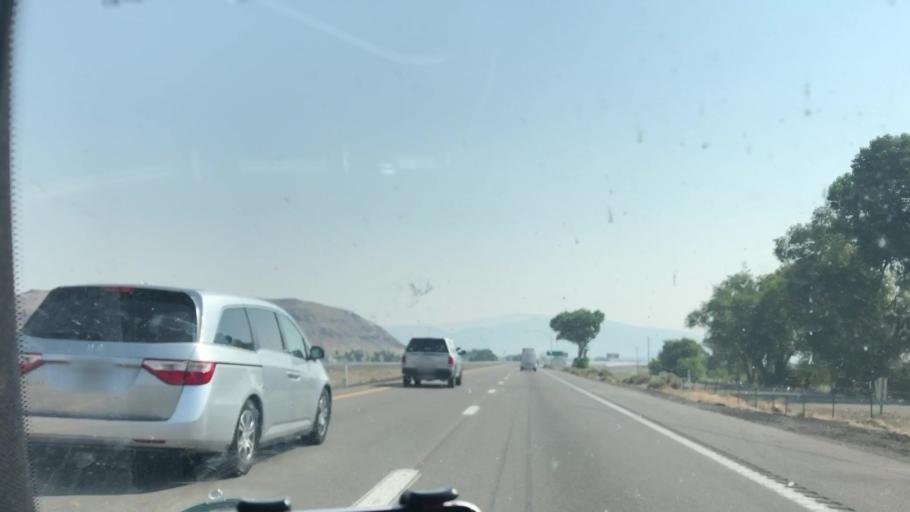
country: US
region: Nevada
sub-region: Lyon County
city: Fernley
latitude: 39.6122
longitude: -119.3162
